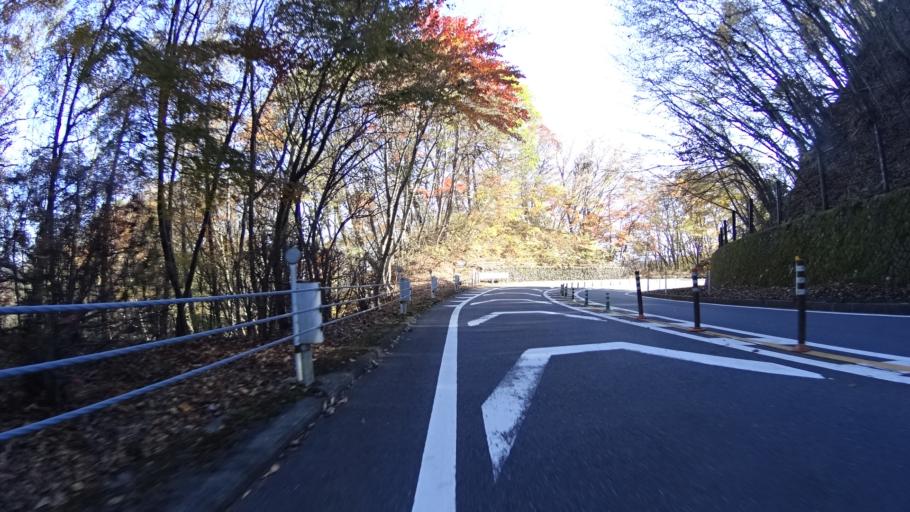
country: JP
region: Yamanashi
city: Uenohara
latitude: 35.7389
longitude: 139.0440
